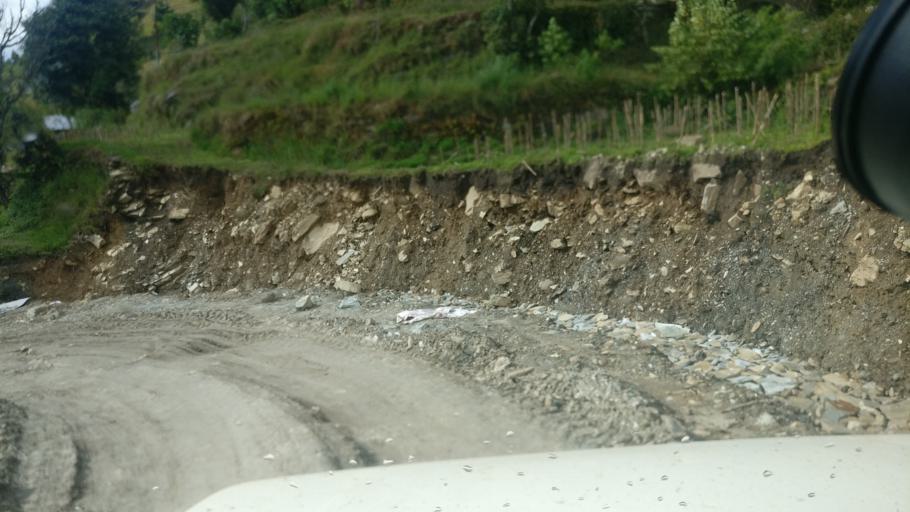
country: NP
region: Western Region
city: Baglung
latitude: 28.2838
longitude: 83.6385
